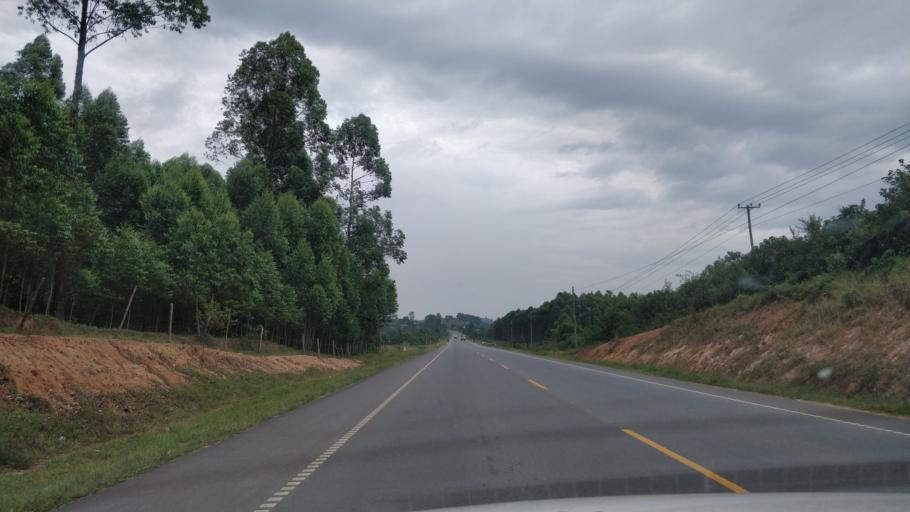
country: UG
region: Western Region
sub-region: Sheema District
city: Kibingo
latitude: -0.6574
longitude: 30.4721
